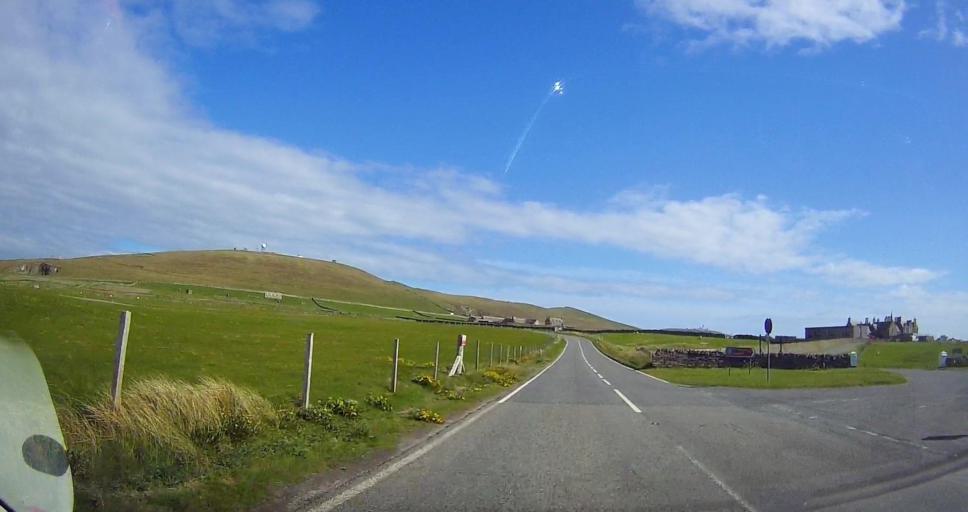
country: GB
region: Scotland
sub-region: Shetland Islands
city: Sandwick
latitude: 59.8721
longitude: -1.2877
